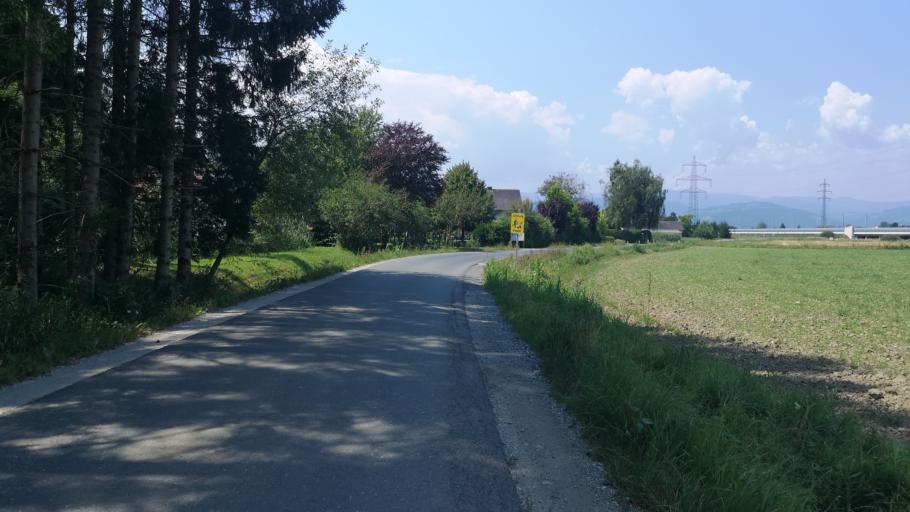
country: AT
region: Styria
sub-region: Politischer Bezirk Deutschlandsberg
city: Gross Sankt Florian
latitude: 46.8143
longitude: 15.3292
